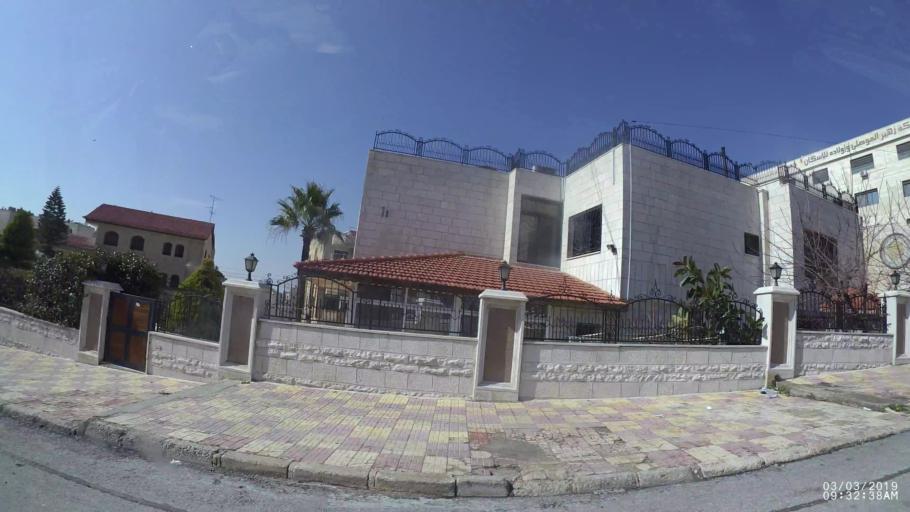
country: JO
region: Amman
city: Al Jubayhah
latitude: 31.9973
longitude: 35.8925
